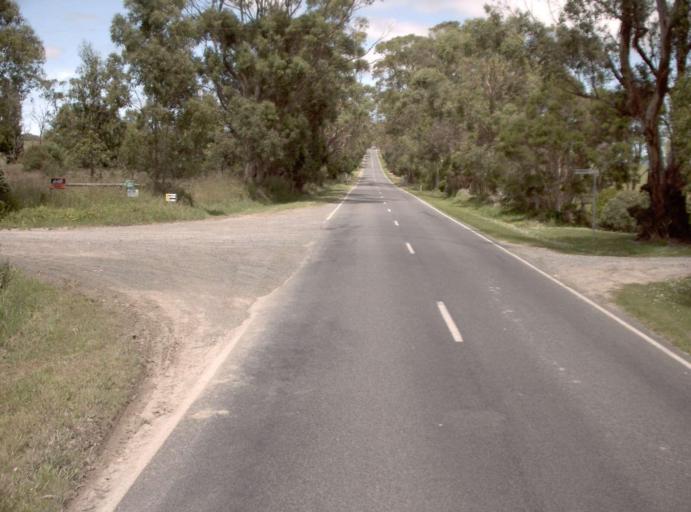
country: AU
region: Victoria
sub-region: Bass Coast
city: North Wonthaggi
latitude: -38.6575
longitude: 146.0189
